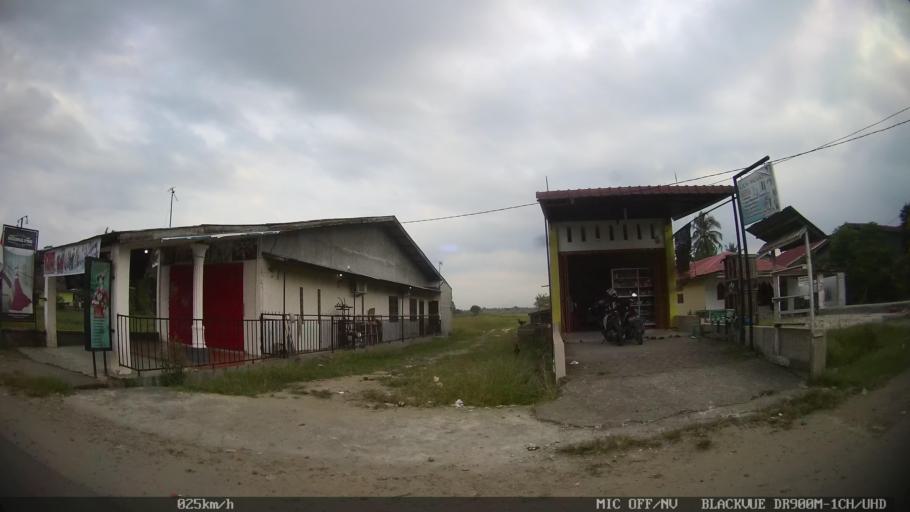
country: ID
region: North Sumatra
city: Sunggal
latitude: 3.5589
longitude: 98.5561
